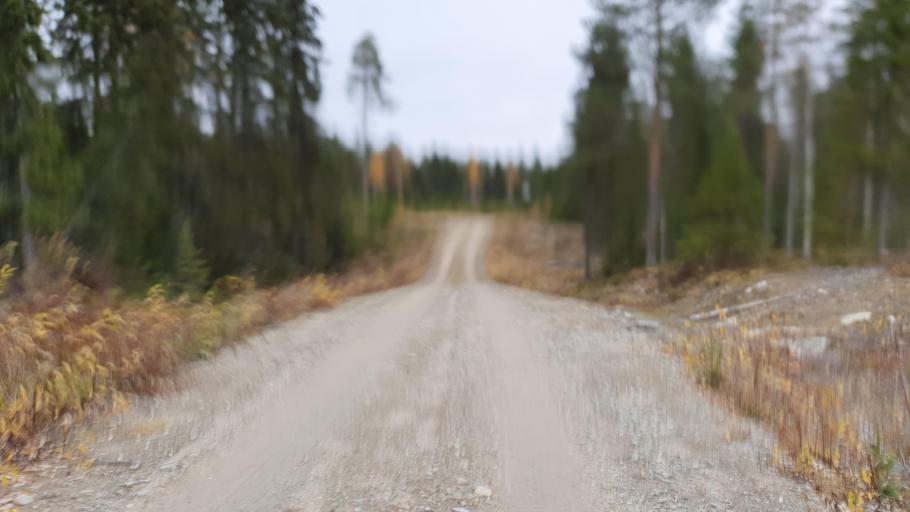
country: FI
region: Kainuu
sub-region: Kehys-Kainuu
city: Kuhmo
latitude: 64.4528
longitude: 29.6256
